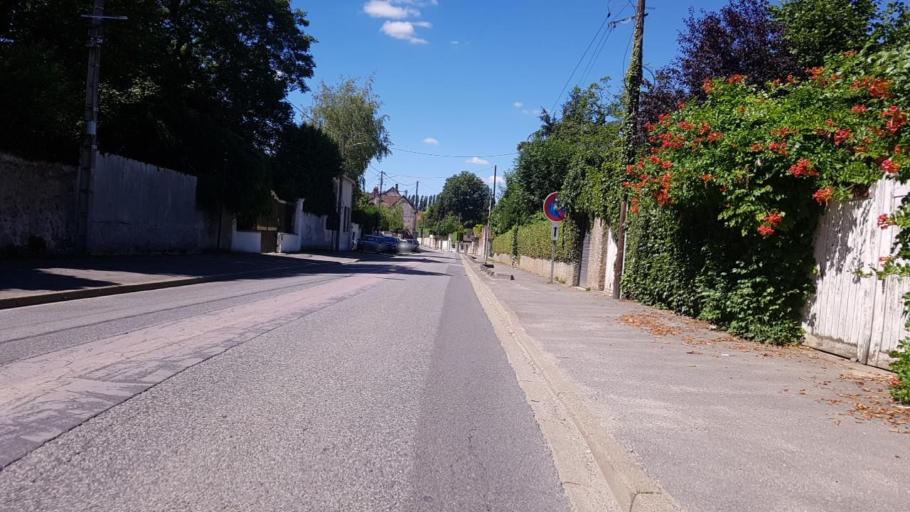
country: FR
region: Ile-de-France
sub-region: Departement de Seine-et-Marne
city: Chamigny
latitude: 48.9617
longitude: 3.1474
